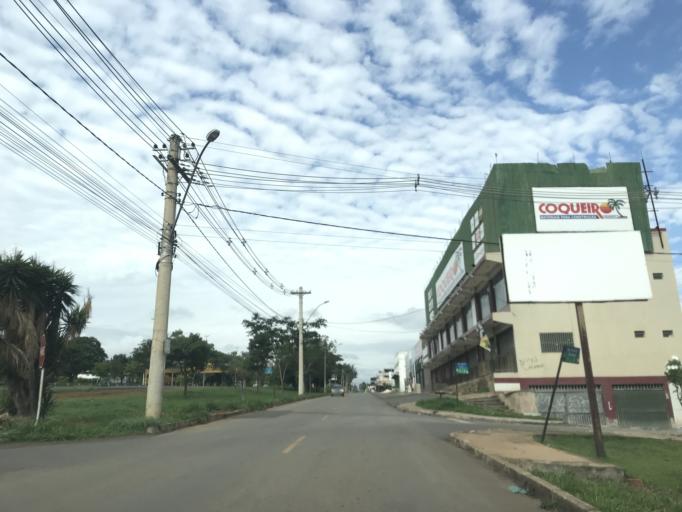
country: BR
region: Federal District
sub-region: Brasilia
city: Brasilia
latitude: -15.6627
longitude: -47.8004
